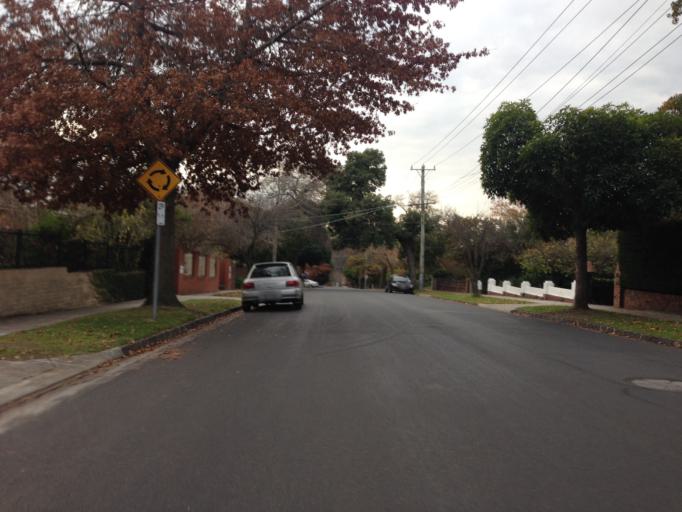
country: AU
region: Victoria
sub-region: Boroondara
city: Kew
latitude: -37.8005
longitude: 145.0325
